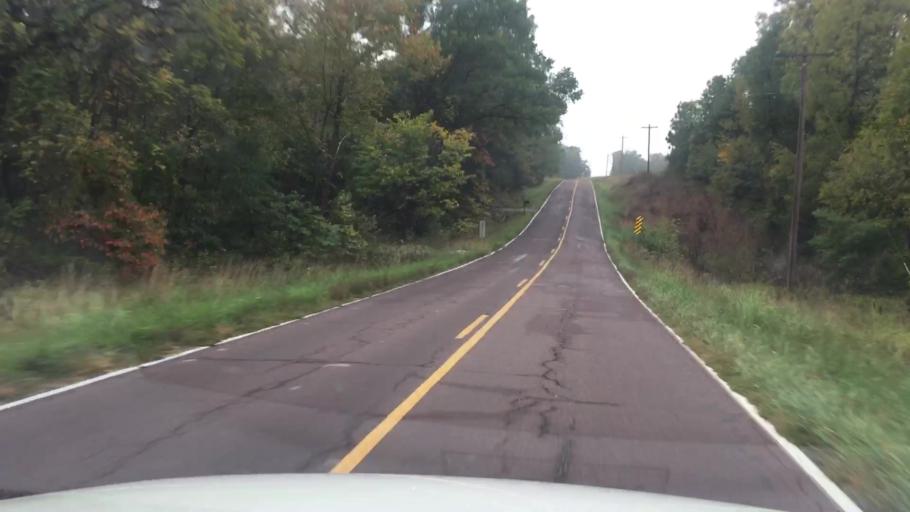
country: US
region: Missouri
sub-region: Boone County
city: Columbia
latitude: 38.8542
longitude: -92.3292
